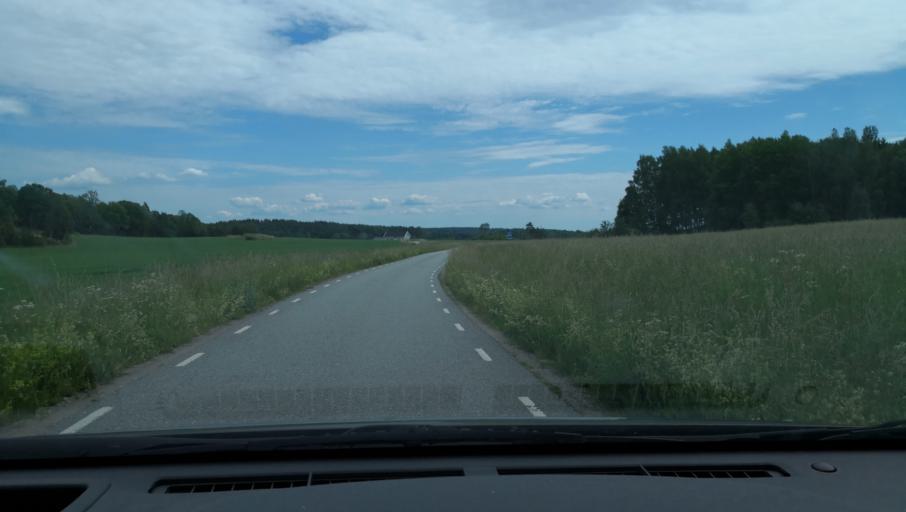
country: SE
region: Uppsala
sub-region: Habo Kommun
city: Balsta
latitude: 59.6935
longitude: 17.4678
